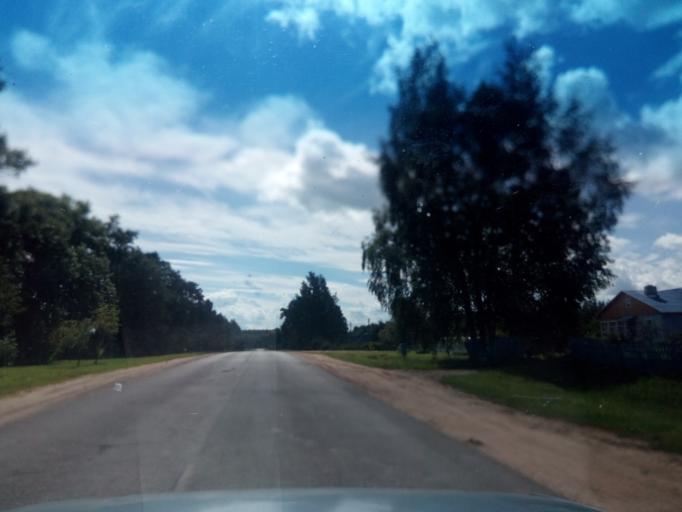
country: BY
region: Vitebsk
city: Dzisna
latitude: 55.6587
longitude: 28.3236
